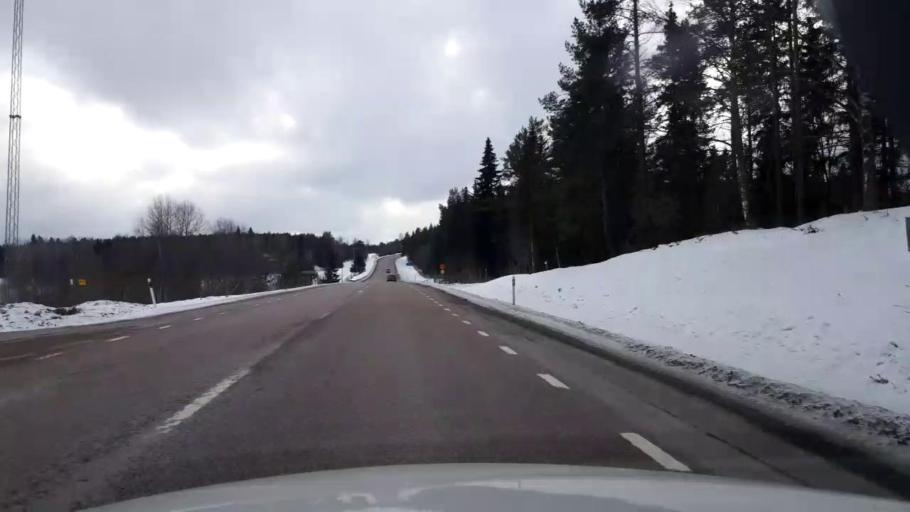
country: SE
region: Gaevleborg
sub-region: Nordanstigs Kommun
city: Bergsjoe
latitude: 61.9239
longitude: 17.2131
